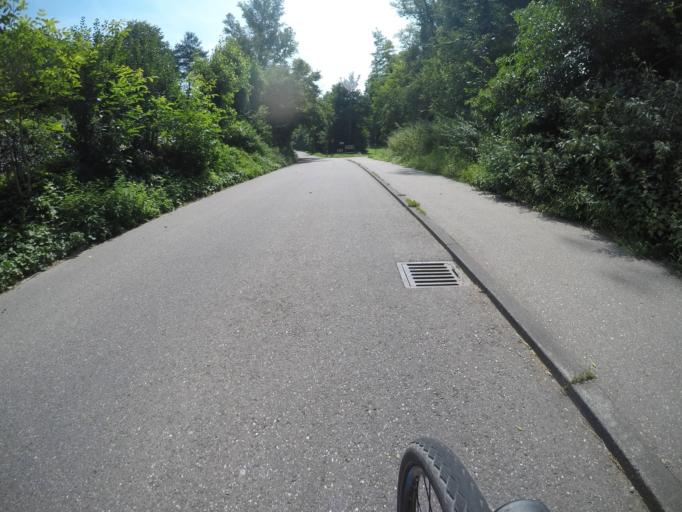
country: DE
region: Baden-Wuerttemberg
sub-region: Karlsruhe Region
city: Bruchsal
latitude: 49.1131
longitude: 8.5989
